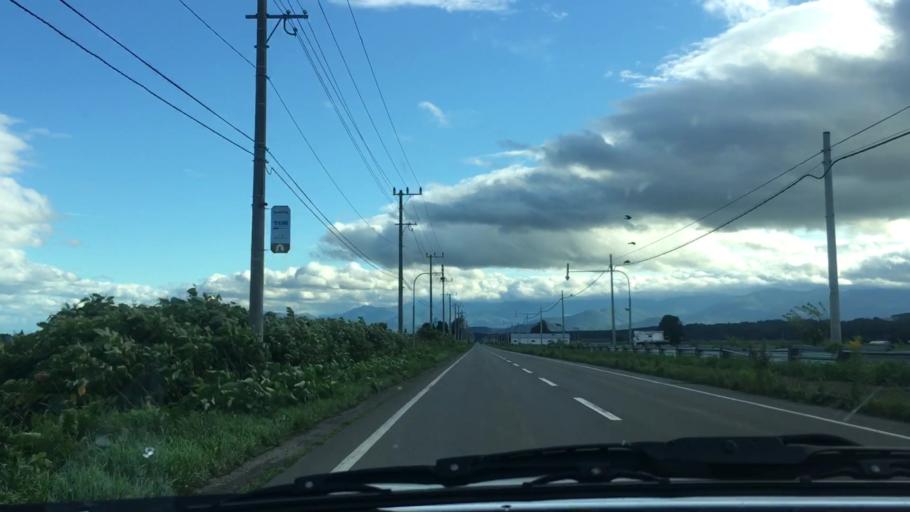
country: JP
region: Hokkaido
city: Otofuke
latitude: 43.1579
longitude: 142.9031
